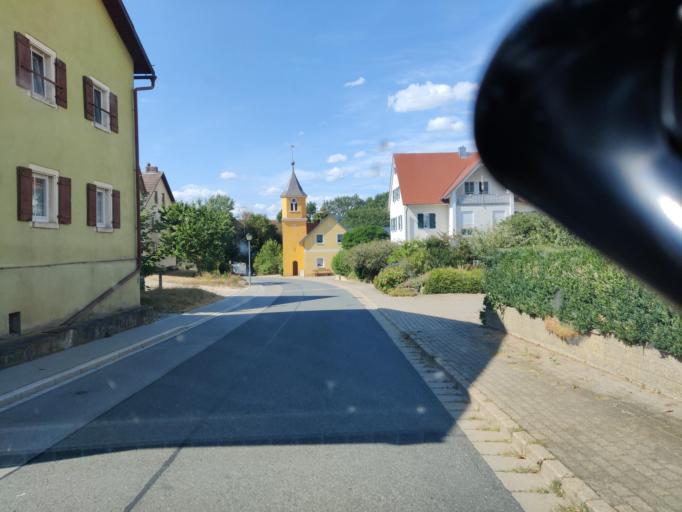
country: DE
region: Bavaria
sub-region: Regierungsbezirk Mittelfranken
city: Thalmassing
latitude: 49.0687
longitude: 11.2245
